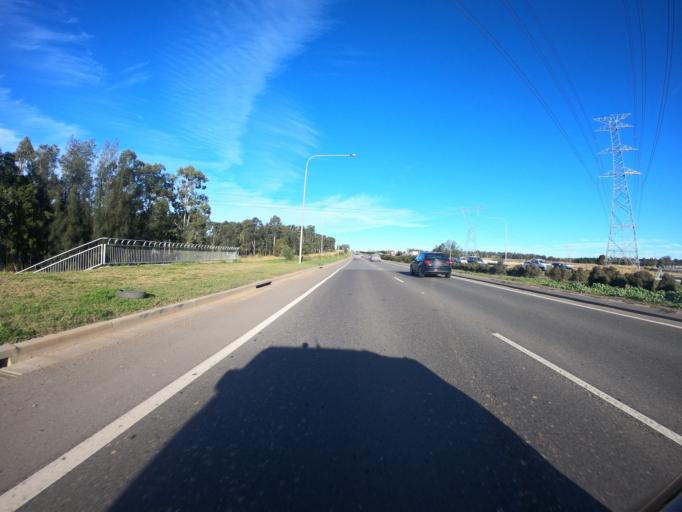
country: AU
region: New South Wales
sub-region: Blacktown
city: Riverstone
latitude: -33.6926
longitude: 150.8273
